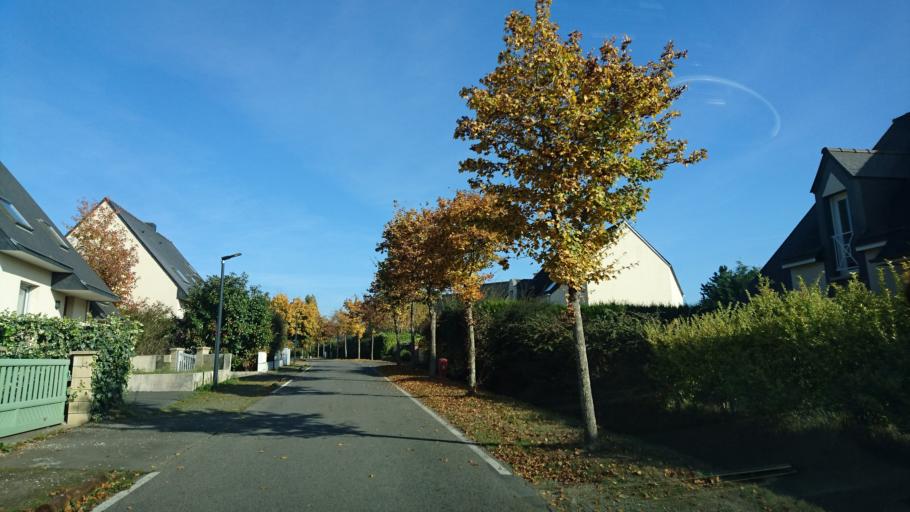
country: FR
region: Brittany
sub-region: Departement d'Ille-et-Vilaine
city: Bruz
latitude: 48.0388
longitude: -1.7605
